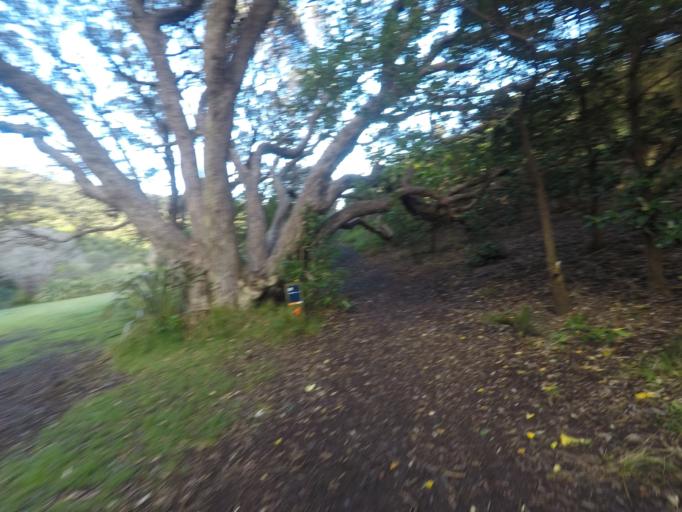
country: NZ
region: Auckland
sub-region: Auckland
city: Muriwai Beach
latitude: -36.9880
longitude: 174.4785
